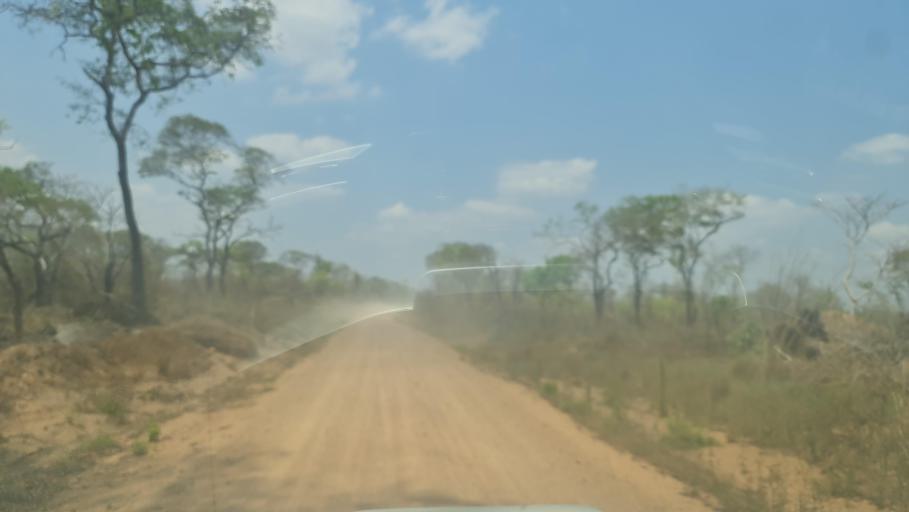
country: MW
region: Southern Region
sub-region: Nsanje District
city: Nsanje
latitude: -17.5608
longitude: 35.8998
